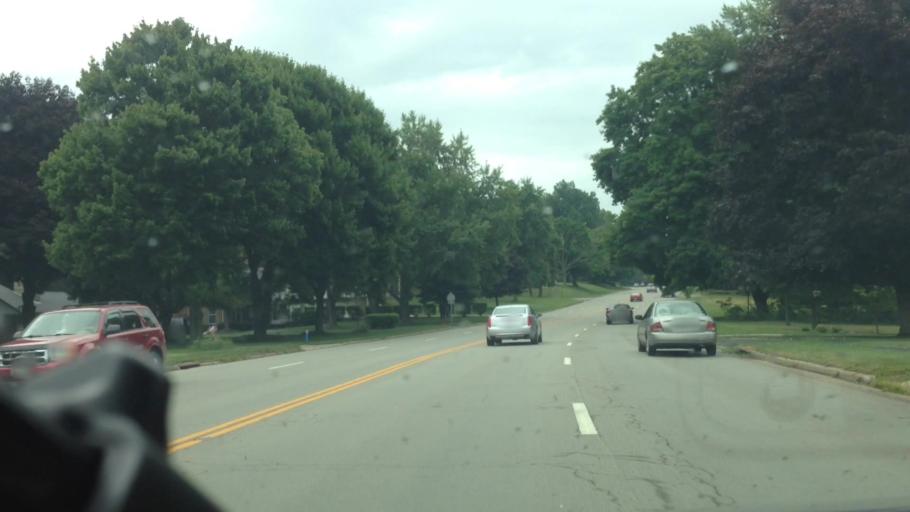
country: US
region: Ohio
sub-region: Stark County
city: North Canton
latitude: 40.8321
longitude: -81.4167
